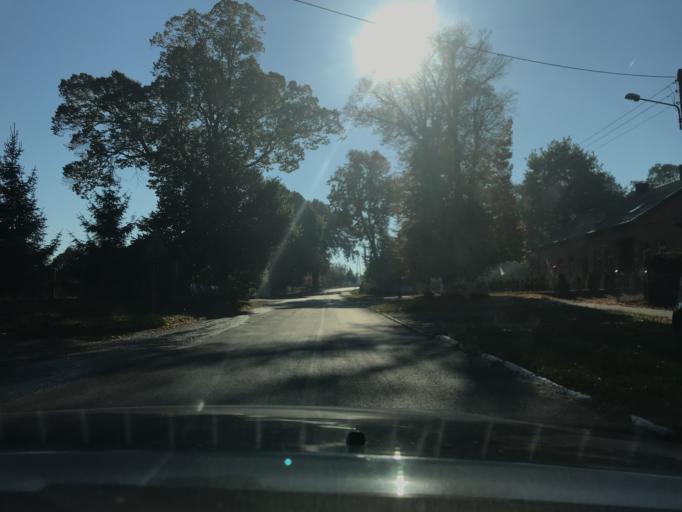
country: PL
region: West Pomeranian Voivodeship
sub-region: Powiat choszczenski
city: Recz
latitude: 53.1870
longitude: 15.5861
